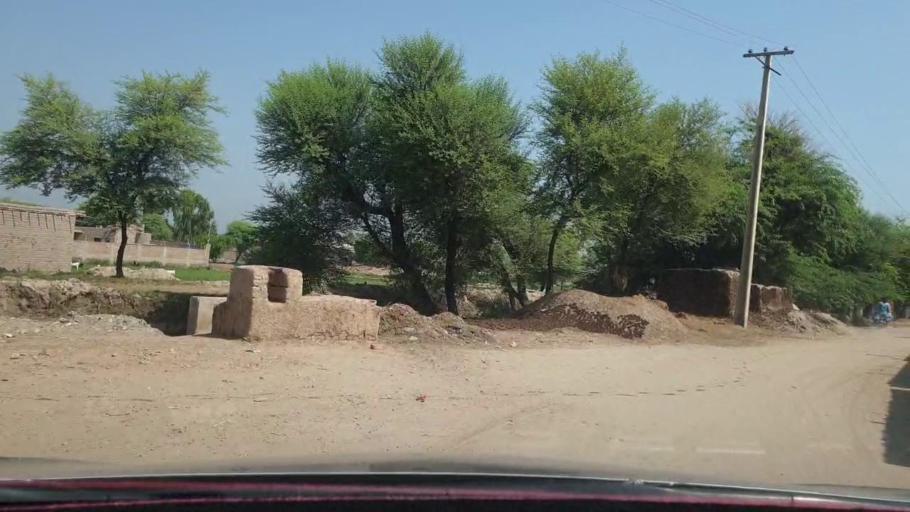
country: PK
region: Sindh
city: Warah
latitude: 27.4814
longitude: 67.8291
